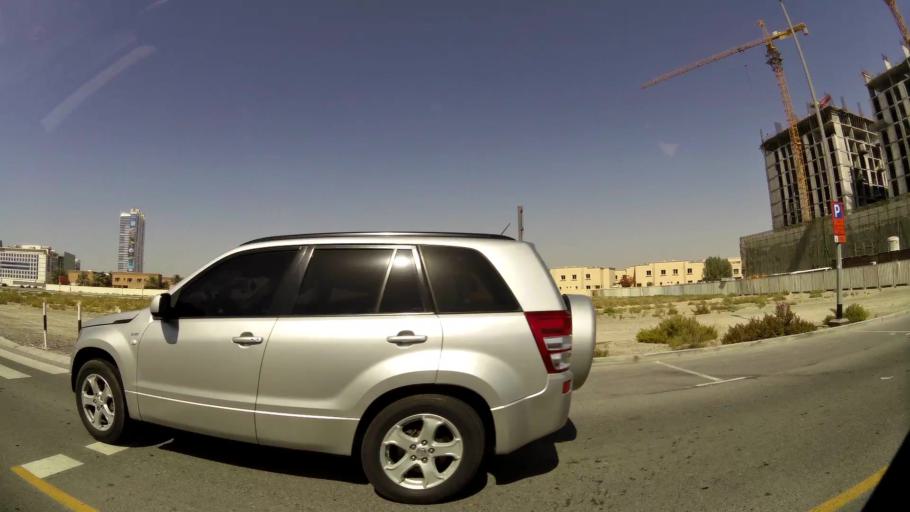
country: AE
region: Dubai
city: Dubai
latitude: 25.1052
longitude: 55.1819
